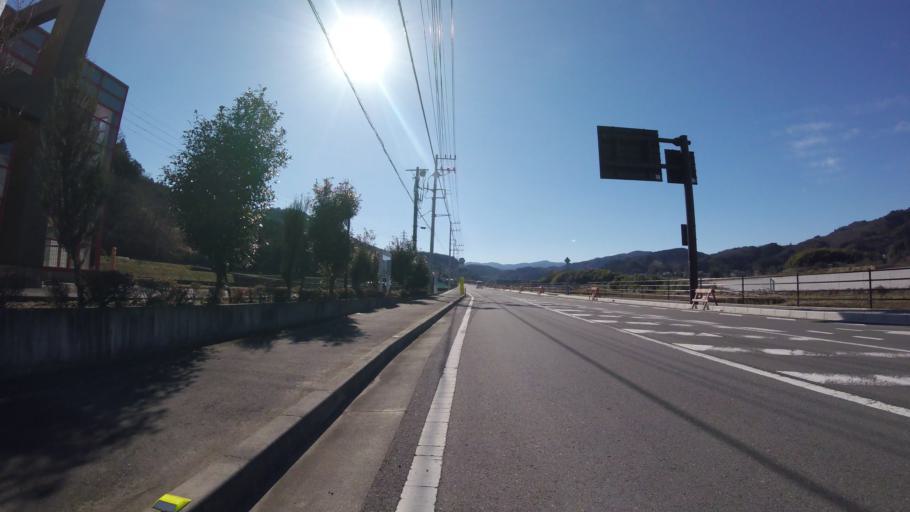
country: JP
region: Shizuoka
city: Ito
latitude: 34.9575
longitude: 138.9445
